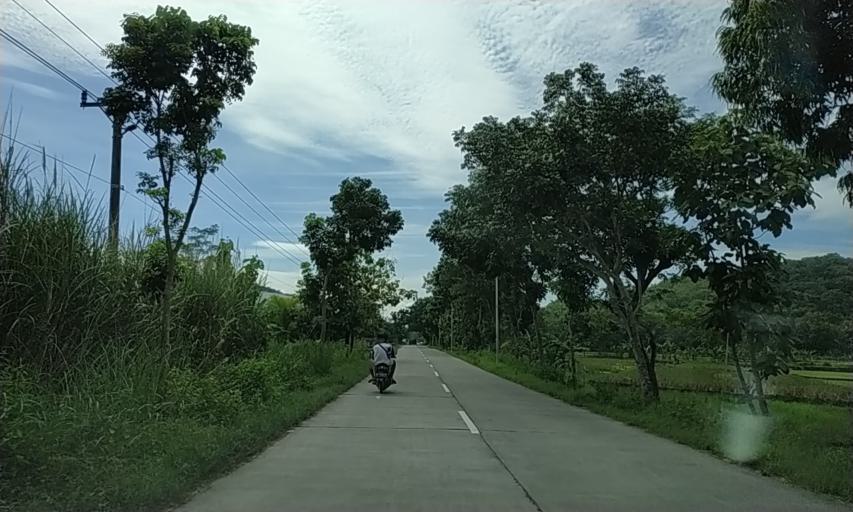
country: ID
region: Central Java
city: Selogiri
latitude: -7.7727
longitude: 110.8440
